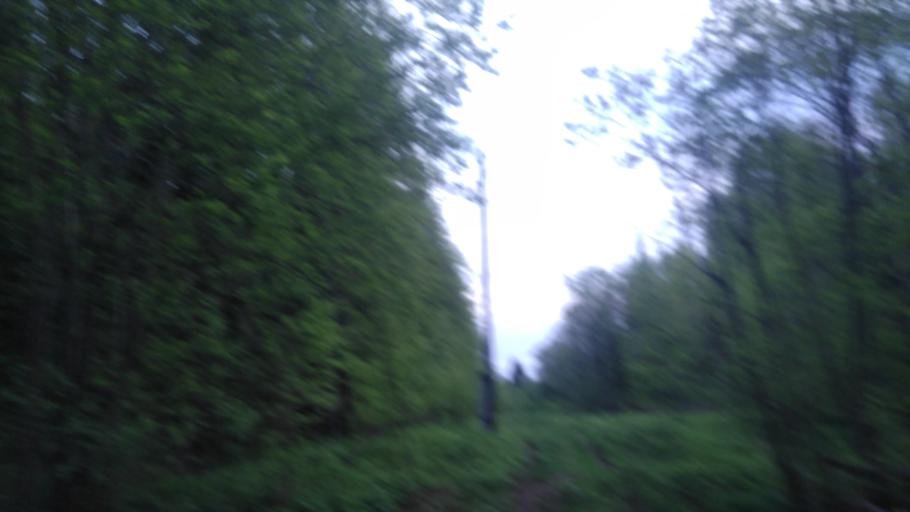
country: RU
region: Perm
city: Froly
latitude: 57.9649
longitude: 56.2906
